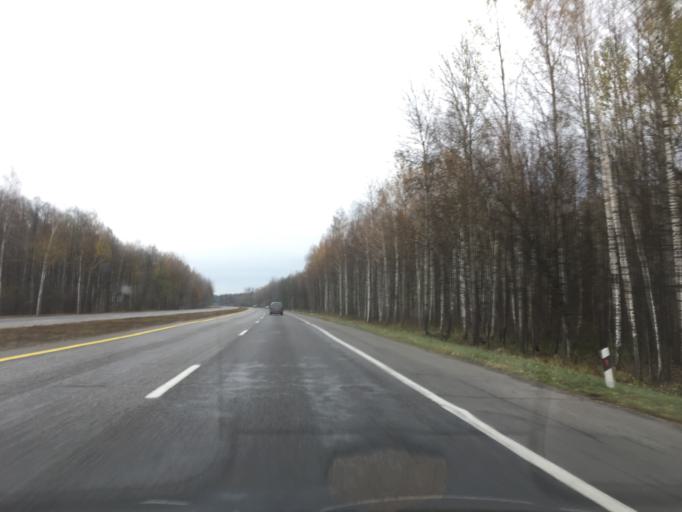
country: BY
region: Gomel
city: Kastsyukowka
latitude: 52.3568
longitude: 30.6911
